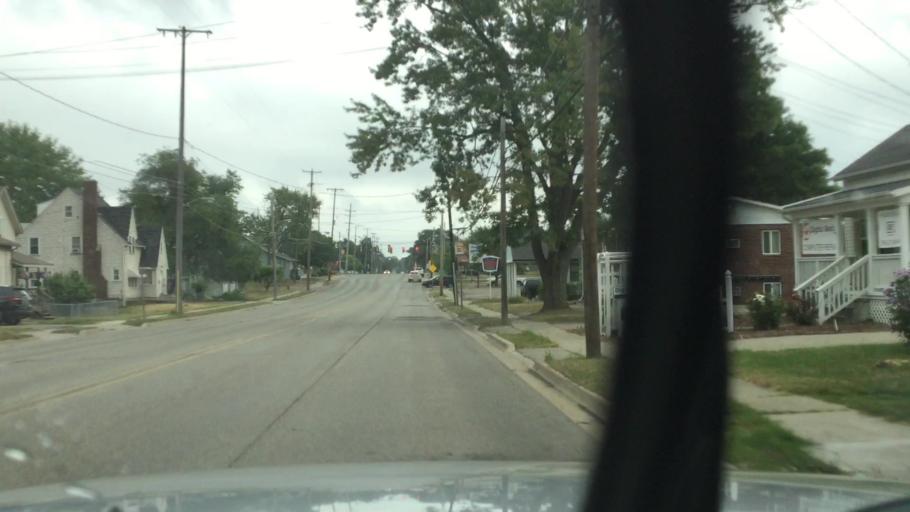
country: US
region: Michigan
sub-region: Genesee County
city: Davison
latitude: 43.0346
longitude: -83.5209
